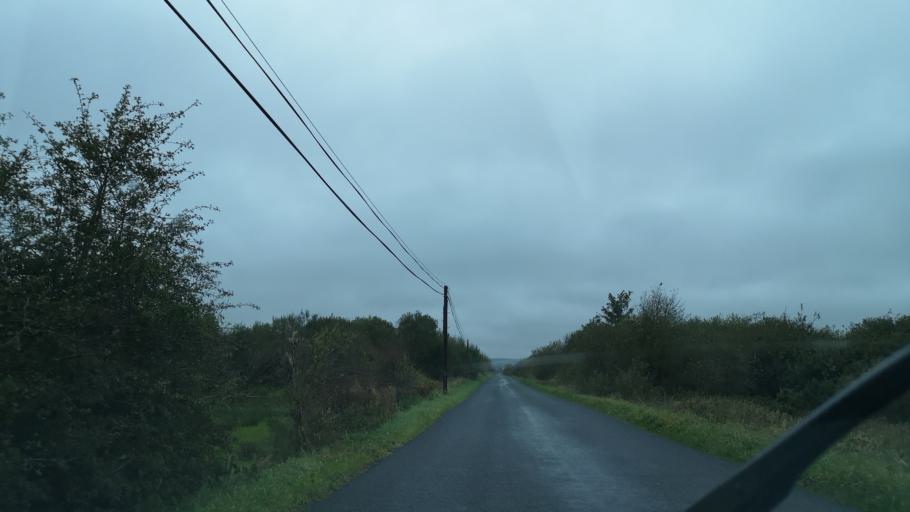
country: IE
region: Connaught
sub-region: Roscommon
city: Ballaghaderreen
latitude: 53.8898
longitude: -8.5714
